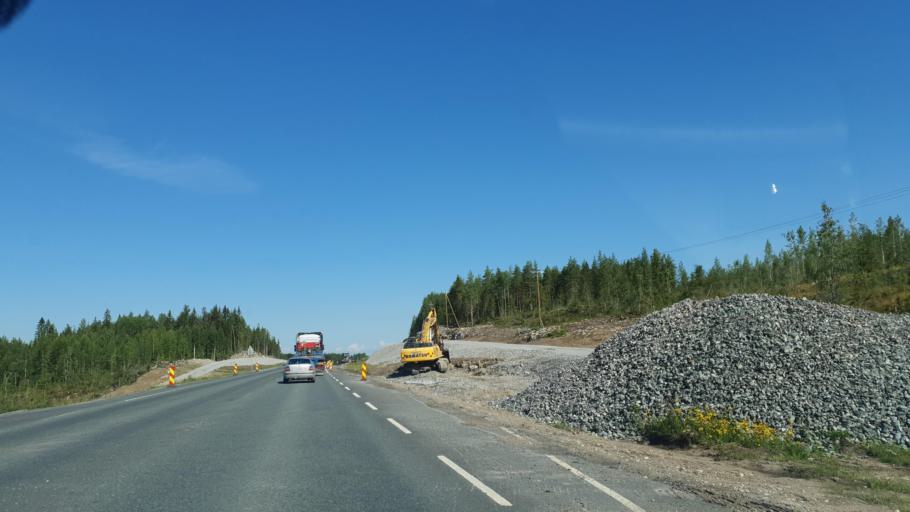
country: FI
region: Northern Savo
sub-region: Ylae-Savo
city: Lapinlahti
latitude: 63.2793
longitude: 27.4570
